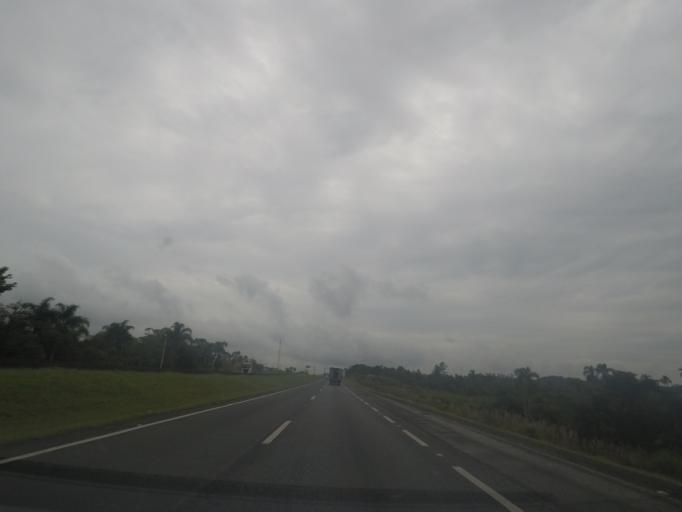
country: BR
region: Sao Paulo
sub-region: Cajati
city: Cajati
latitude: -24.9348
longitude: -48.2885
